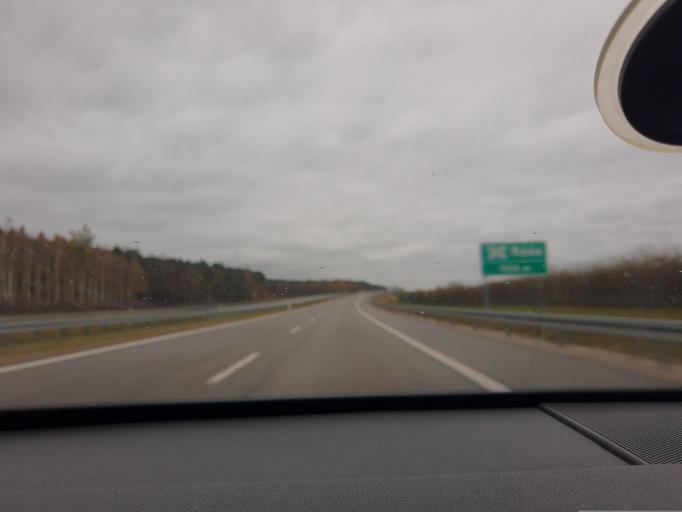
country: PL
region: Lodz Voivodeship
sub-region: Powiat pabianicki
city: Dobron
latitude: 51.6212
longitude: 19.2744
